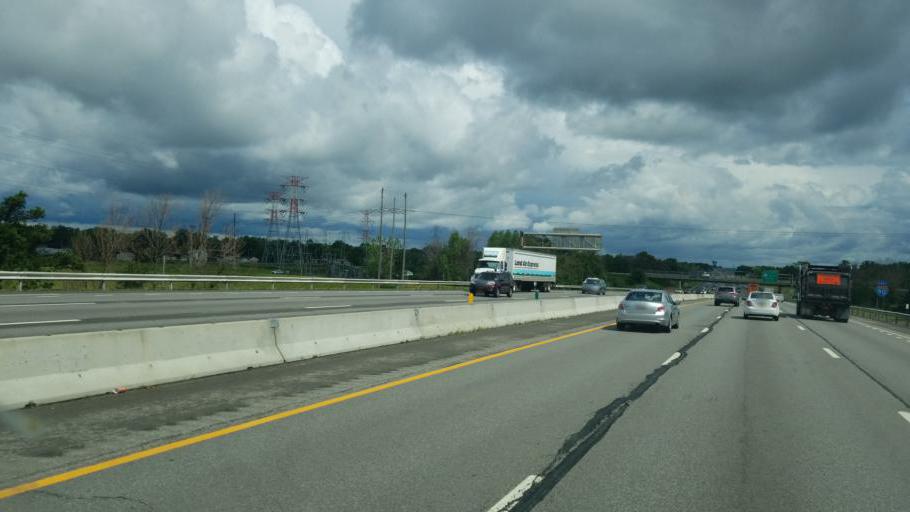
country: US
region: New York
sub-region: Erie County
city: Cheektowaga
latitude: 42.9159
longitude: -78.7662
